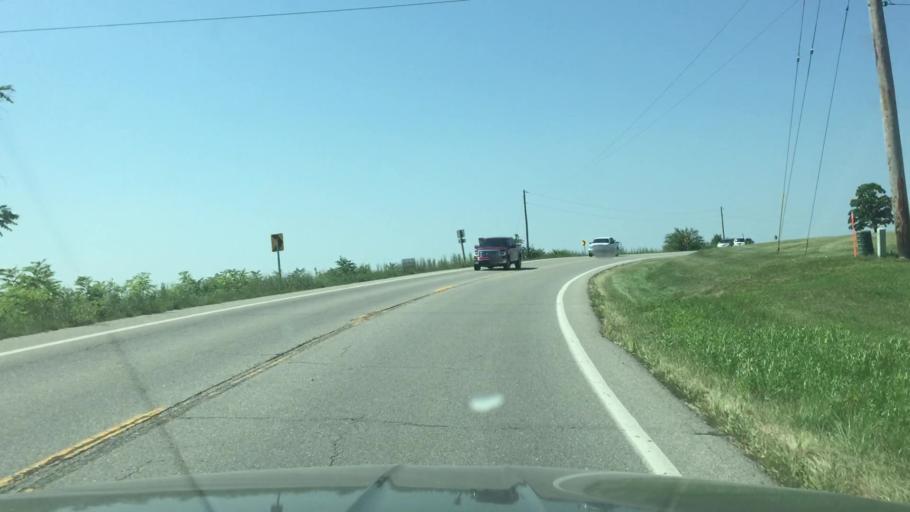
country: US
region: Missouri
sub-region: Moniteau County
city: Tipton
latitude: 38.6438
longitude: -92.7843
